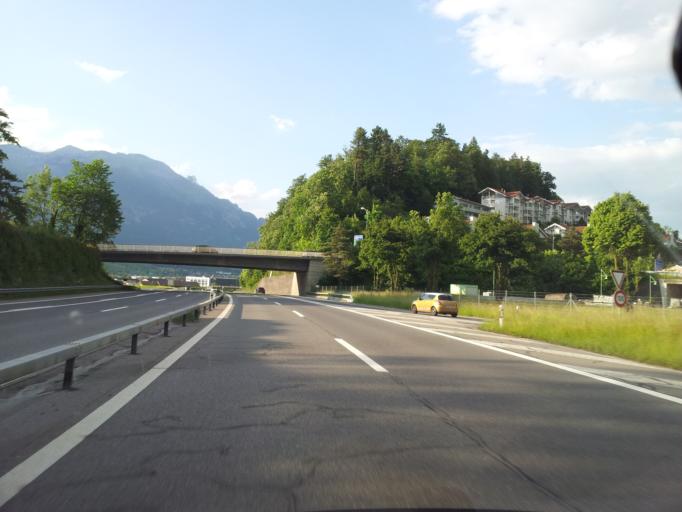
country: CH
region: Obwalden
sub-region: Obwalden
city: Sarnen
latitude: 46.8957
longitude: 8.2576
